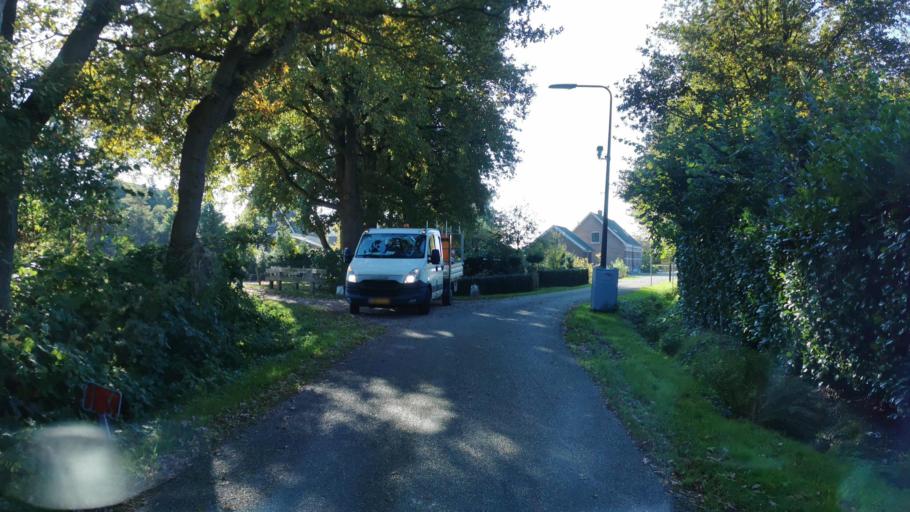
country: NL
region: Overijssel
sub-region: Gemeente Enschede
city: Enschede
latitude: 52.2557
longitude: 6.9147
